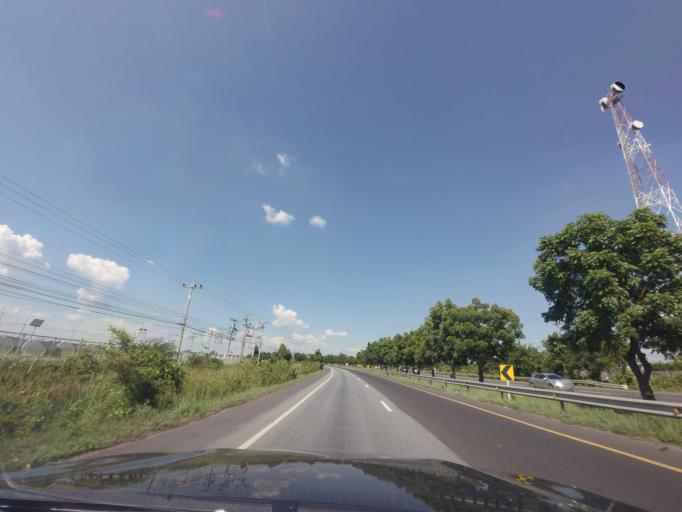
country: TH
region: Nakhon Ratchasima
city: Non Sung
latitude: 15.1905
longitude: 102.3466
